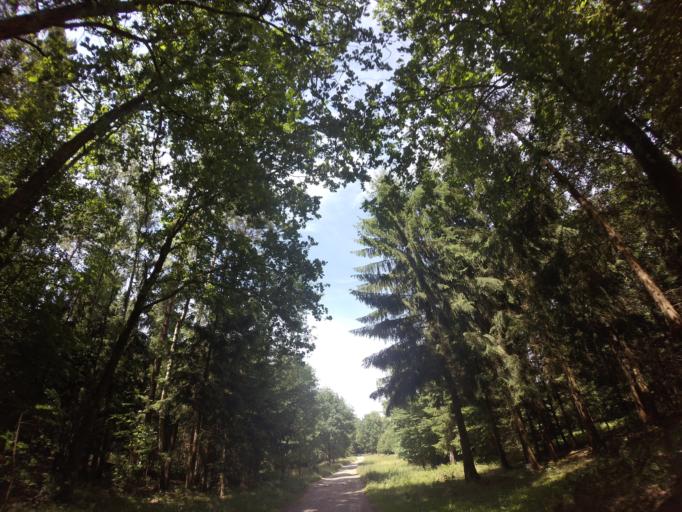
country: PL
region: West Pomeranian Voivodeship
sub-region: Powiat choszczenski
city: Recz
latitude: 53.3326
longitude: 15.5230
